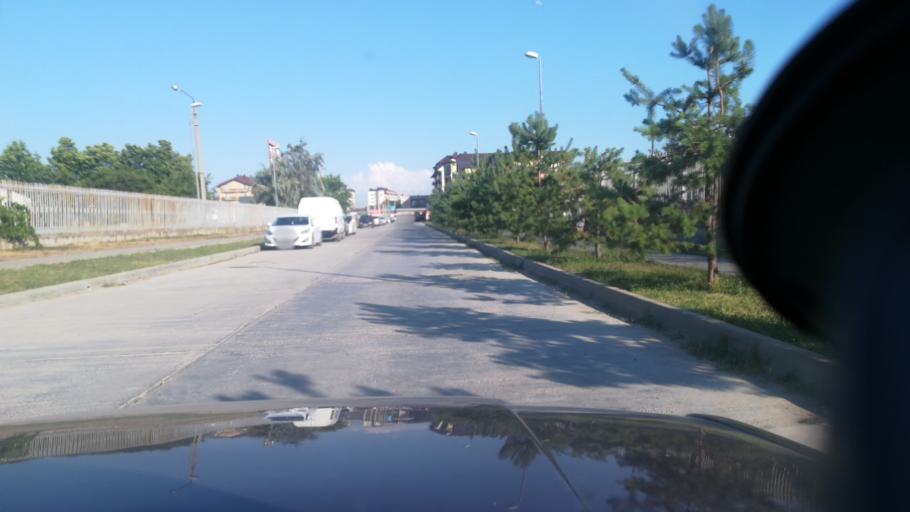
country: RU
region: Krasnodarskiy
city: Vityazevo
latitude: 44.9886
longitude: 37.2487
